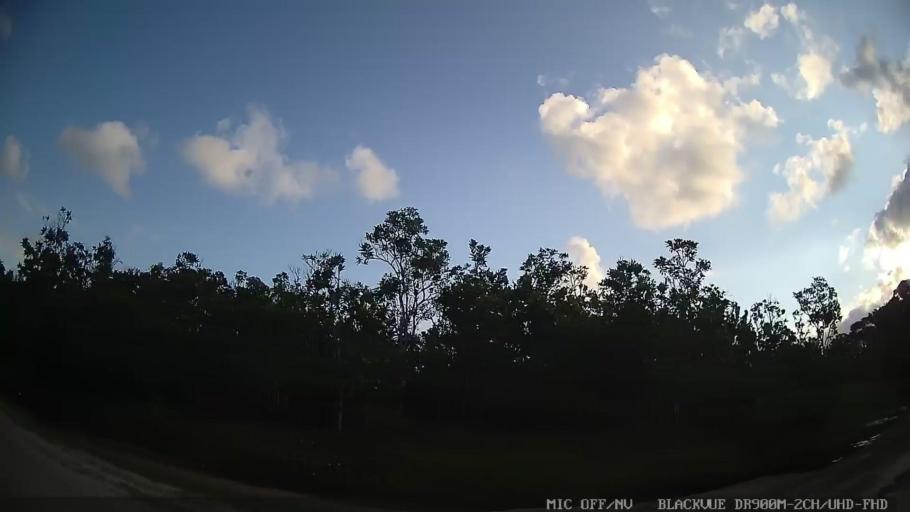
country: BR
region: Sao Paulo
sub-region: Itanhaem
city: Itanhaem
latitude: -24.1642
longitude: -46.8412
